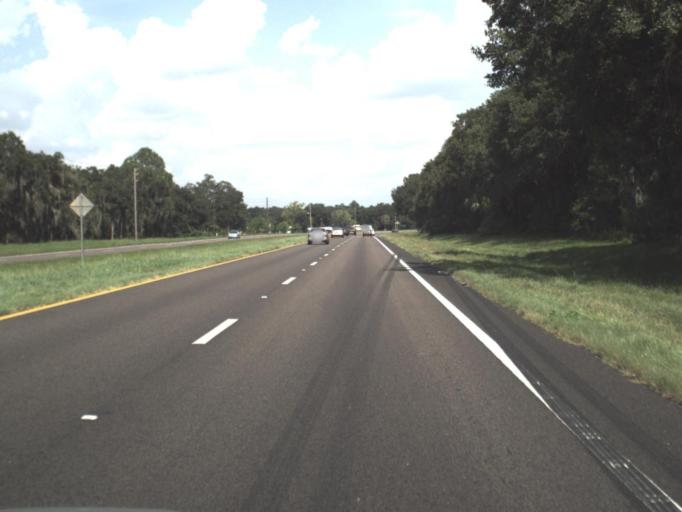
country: US
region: Florida
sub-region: Polk County
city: Willow Oak
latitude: 27.9377
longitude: -82.0949
